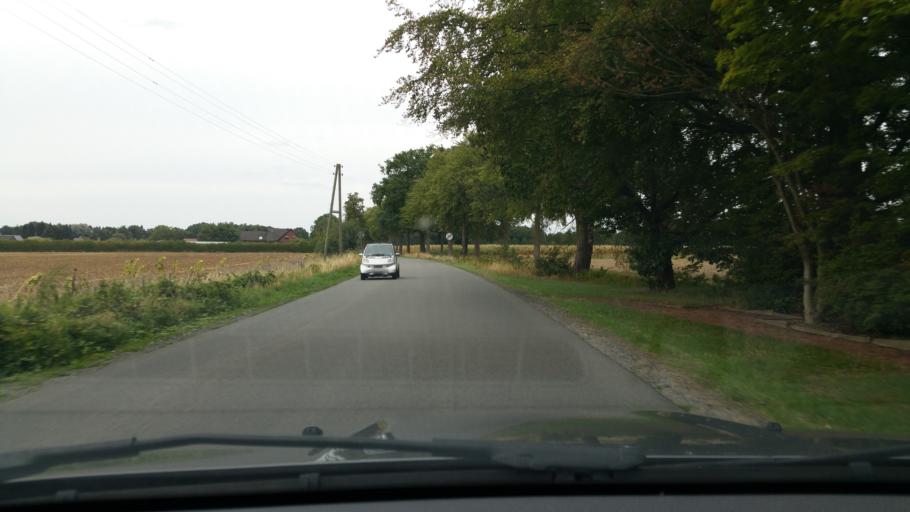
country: DE
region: North Rhine-Westphalia
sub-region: Regierungsbezirk Dusseldorf
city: Bocholt
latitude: 51.8606
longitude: 6.6360
